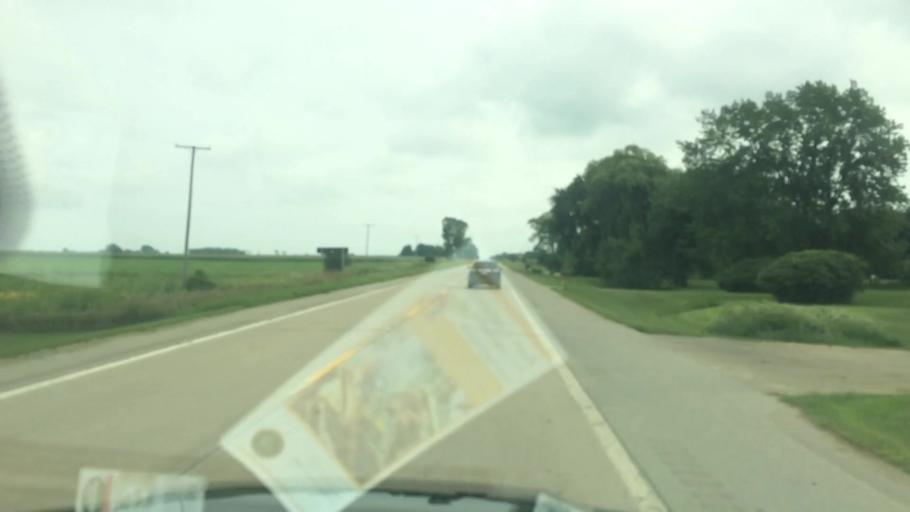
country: US
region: Michigan
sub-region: Huron County
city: Bad Axe
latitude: 44.0424
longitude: -82.9472
